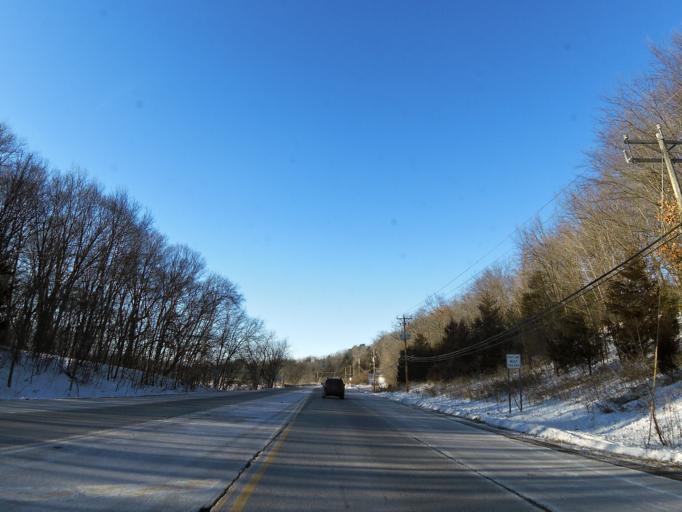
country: US
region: Minnesota
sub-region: Carver County
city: Victoria
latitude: 44.8885
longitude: -93.6576
